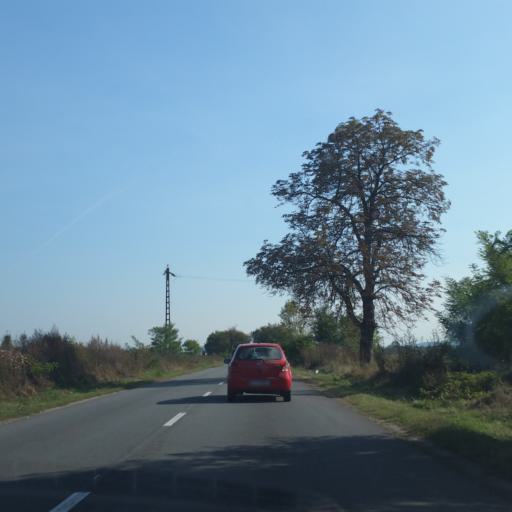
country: RO
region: Arges
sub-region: Comuna Merisani
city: Merisani
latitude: 45.0079
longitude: 24.7266
